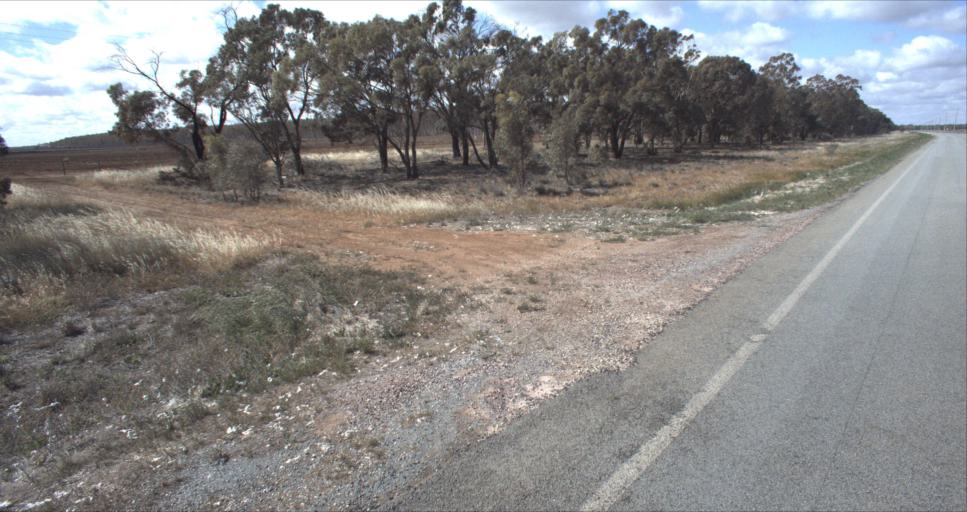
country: AU
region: New South Wales
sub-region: Murrumbidgee Shire
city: Darlington Point
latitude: -34.5782
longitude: 146.1656
